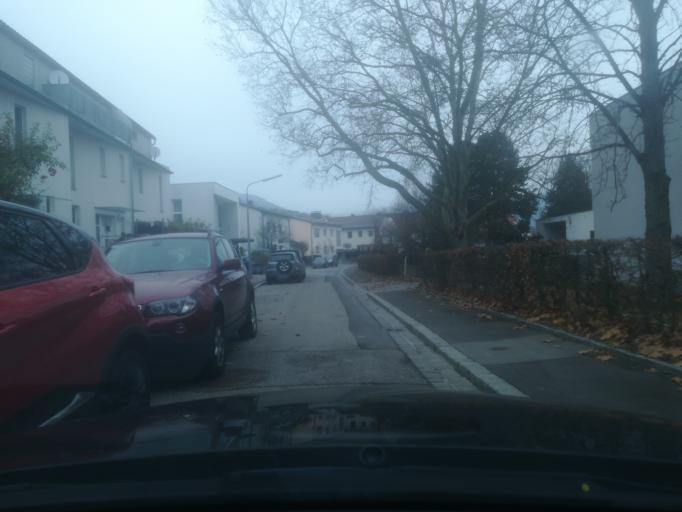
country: AT
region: Upper Austria
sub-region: Linz Stadt
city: Linz
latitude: 48.3289
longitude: 14.2816
